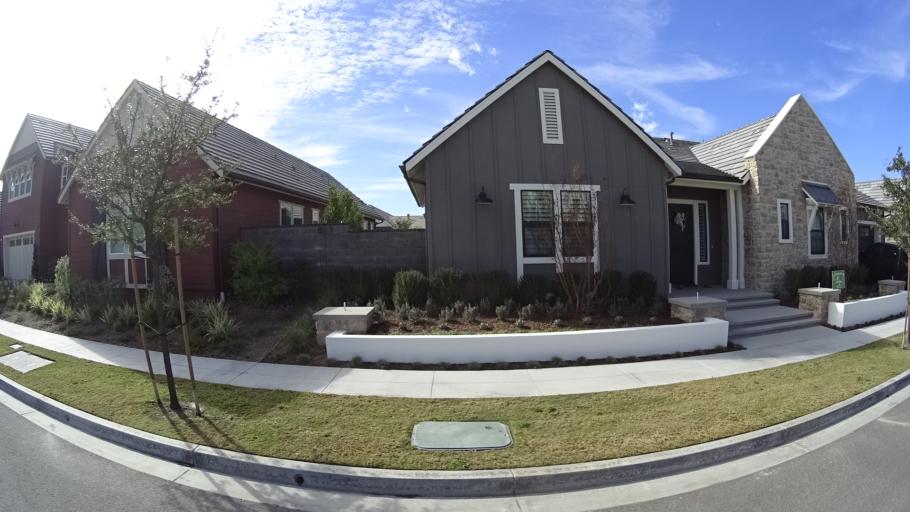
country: US
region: California
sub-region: Orange County
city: Ladera Ranch
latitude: 33.5495
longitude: -117.5996
